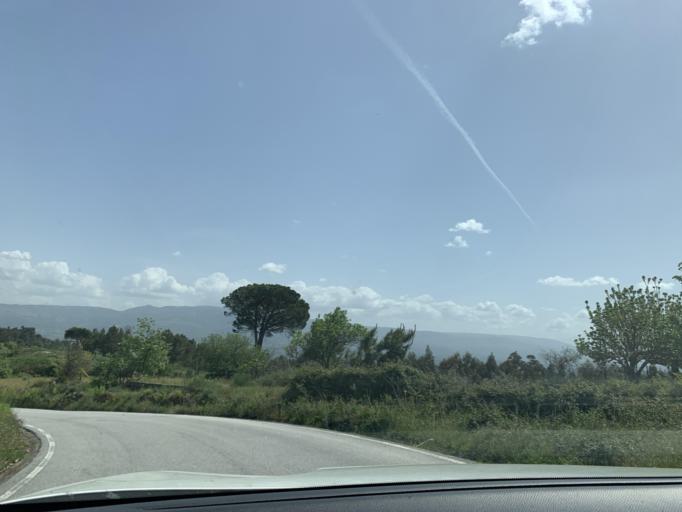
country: PT
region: Guarda
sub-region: Fornos de Algodres
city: Fornos de Algodres
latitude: 40.5963
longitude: -7.6327
